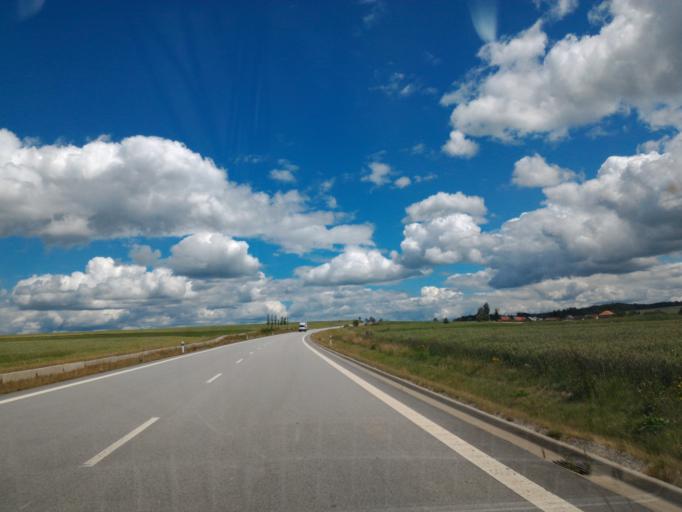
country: CZ
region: Vysocina
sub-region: Okres Jihlava
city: Polna
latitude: 49.4331
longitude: 15.7175
